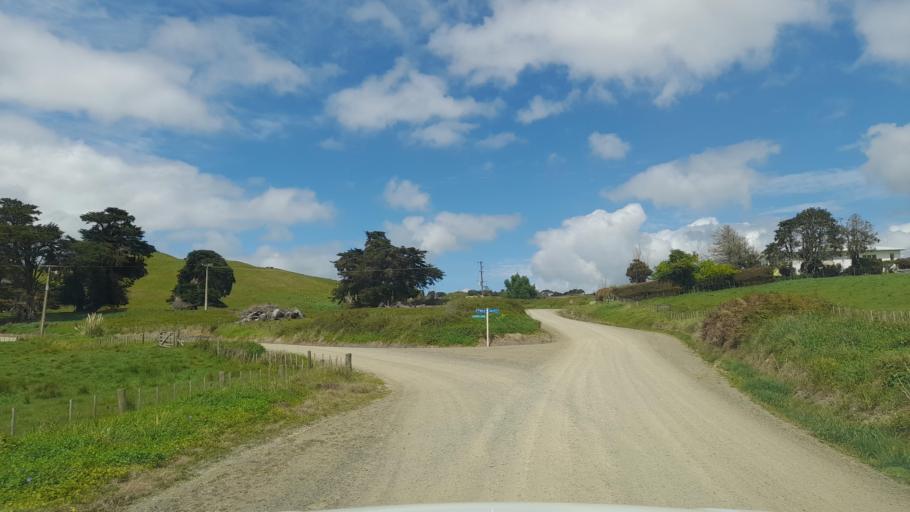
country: NZ
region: Auckland
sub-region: Auckland
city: Wellsford
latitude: -36.1807
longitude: 174.3156
